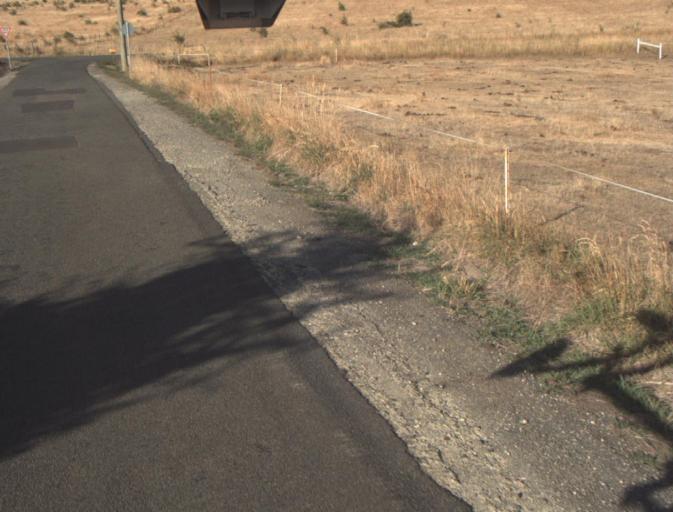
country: AU
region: Tasmania
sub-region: Launceston
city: Newstead
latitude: -41.4375
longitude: 147.2104
